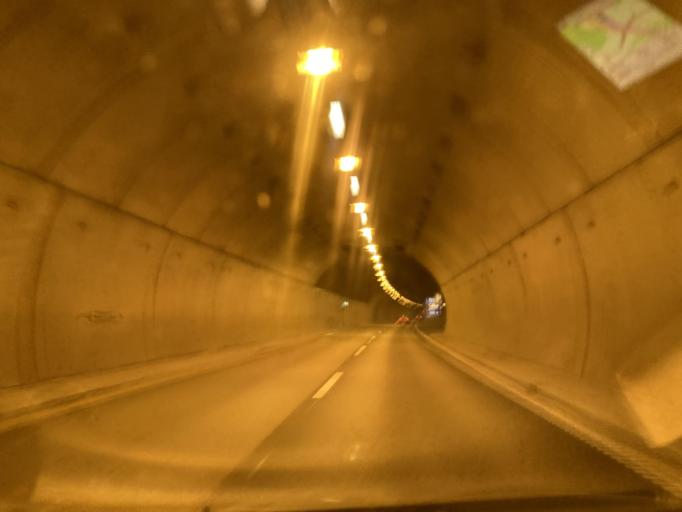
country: NO
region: Akershus
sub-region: Eidsvoll
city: Eidsvoll
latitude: 60.3447
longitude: 11.2070
